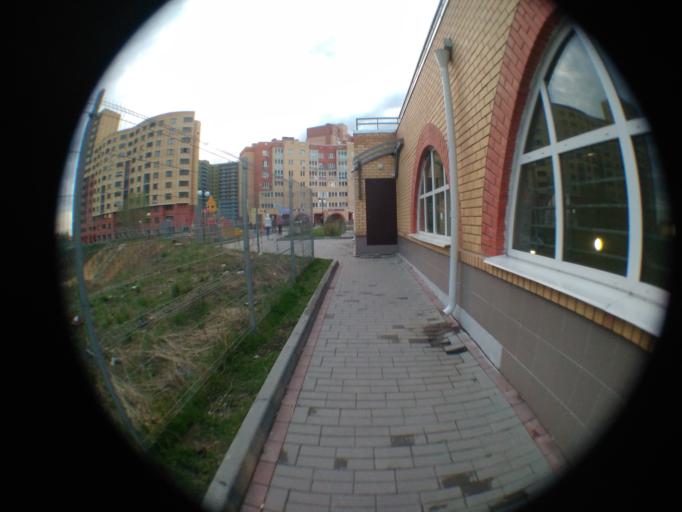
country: RU
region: Moskovskaya
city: Bykovo
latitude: 55.6028
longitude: 38.0864
